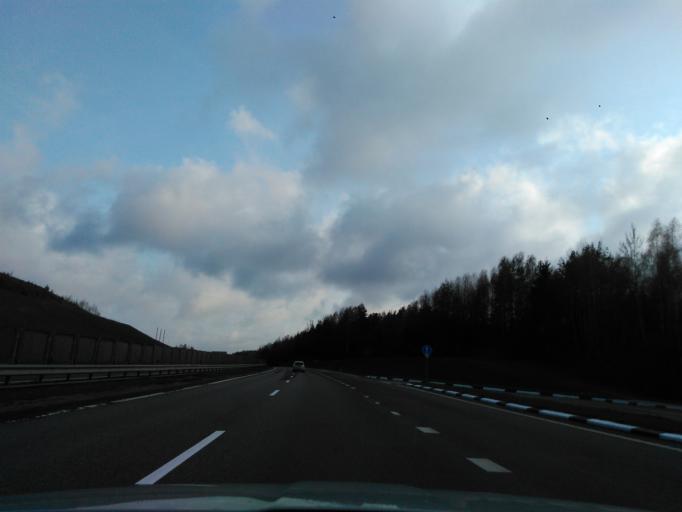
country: BY
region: Minsk
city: Lahoysk
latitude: 54.2031
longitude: 27.8185
